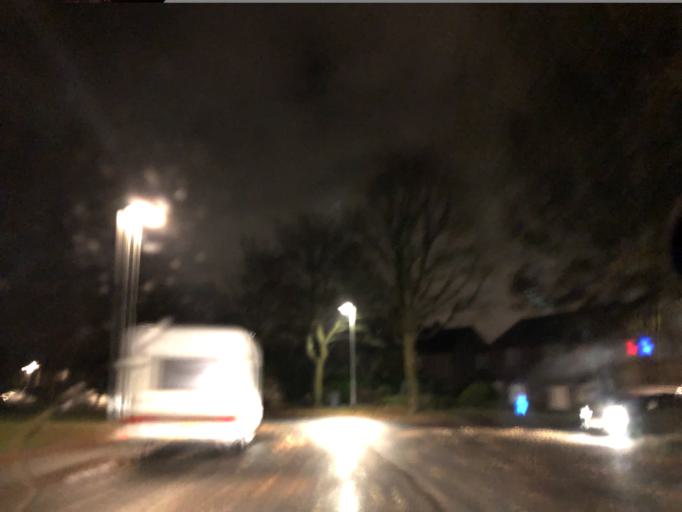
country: GB
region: England
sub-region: Borough of Oldham
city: Shaw
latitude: 53.5510
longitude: -2.0845
